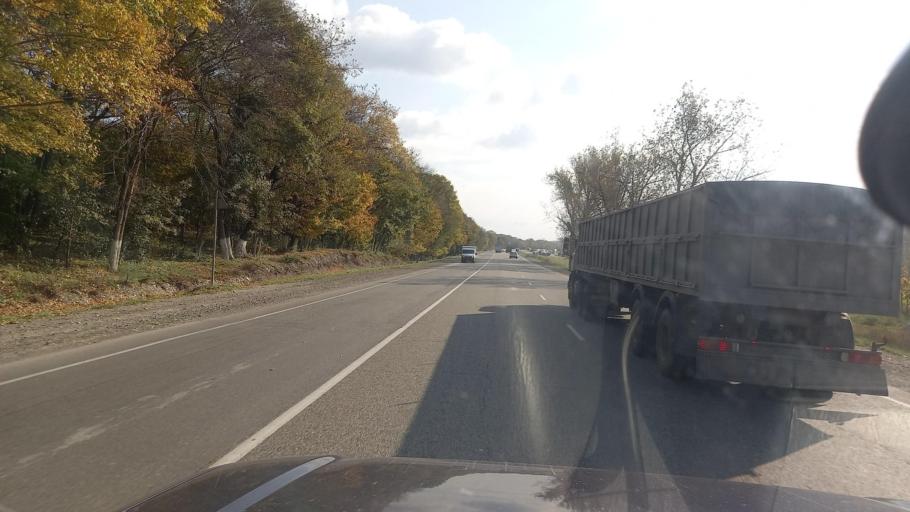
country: RU
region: Krasnodarskiy
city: Gayduk
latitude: 44.8742
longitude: 37.7927
